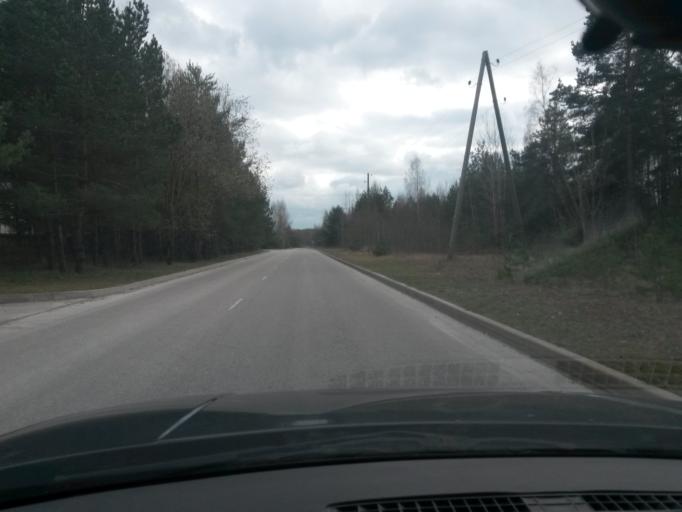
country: LV
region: Stopini
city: Ulbroka
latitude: 56.8999
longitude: 24.2471
